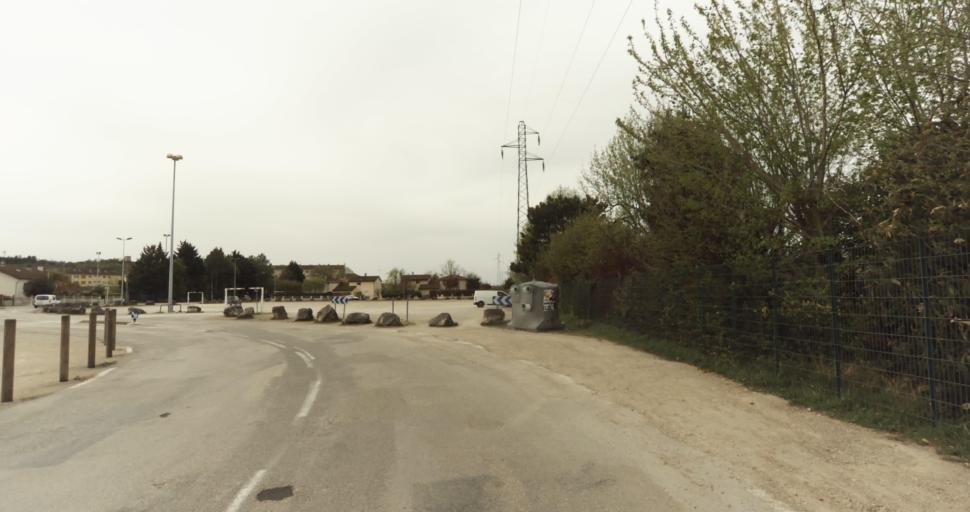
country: FR
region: Rhone-Alpes
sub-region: Departement de l'Ain
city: Amberieu-en-Bugey
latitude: 45.9612
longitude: 5.3410
